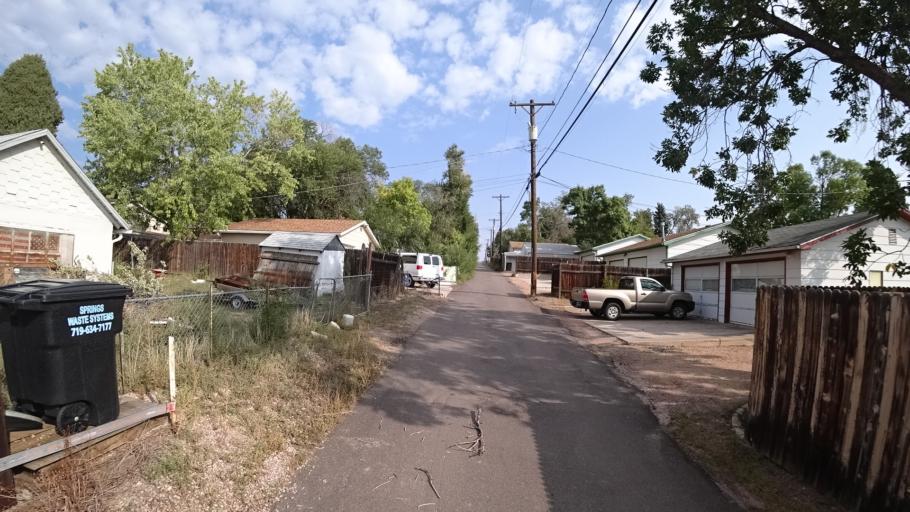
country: US
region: Colorado
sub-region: El Paso County
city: Colorado Springs
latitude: 38.8479
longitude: -104.7866
